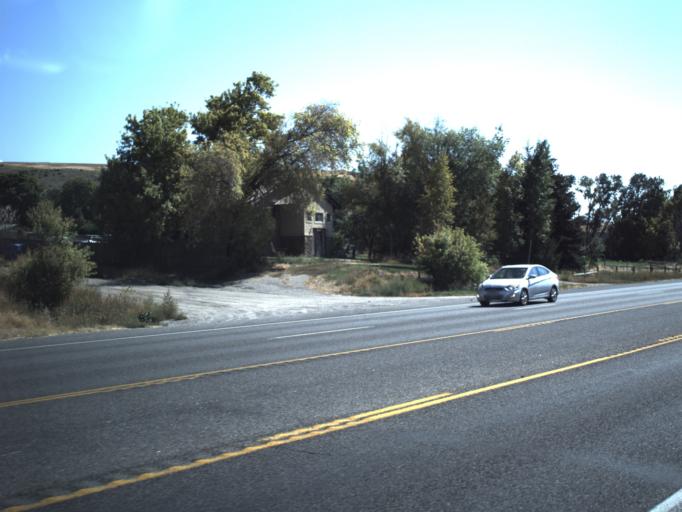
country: US
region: Utah
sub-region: Cache County
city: Smithfield
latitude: 41.8653
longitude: -111.8294
